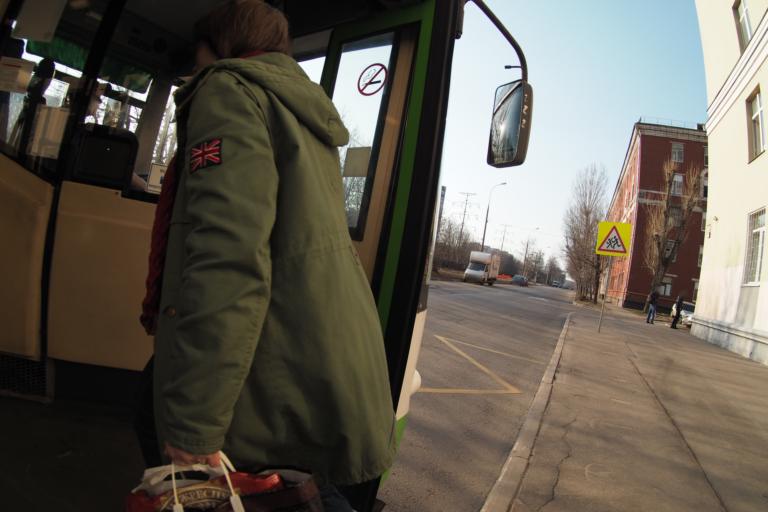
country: RU
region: Moskovskaya
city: Bol'shaya Setun'
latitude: 55.7180
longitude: 37.3966
